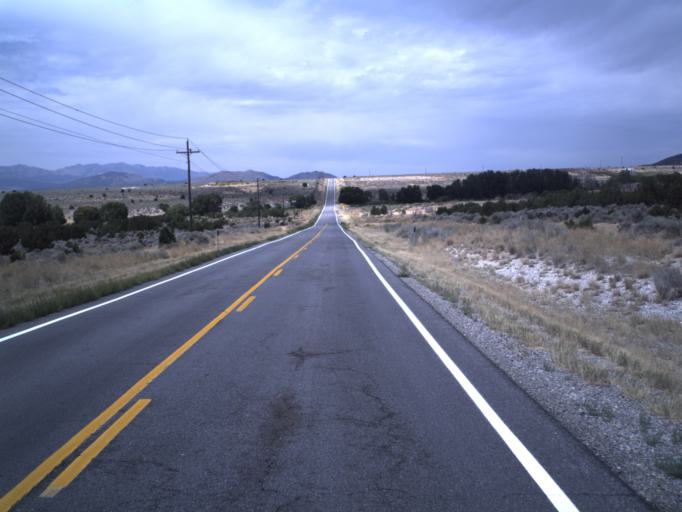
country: US
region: Utah
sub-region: Tooele County
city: Tooele
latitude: 40.3390
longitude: -112.3015
